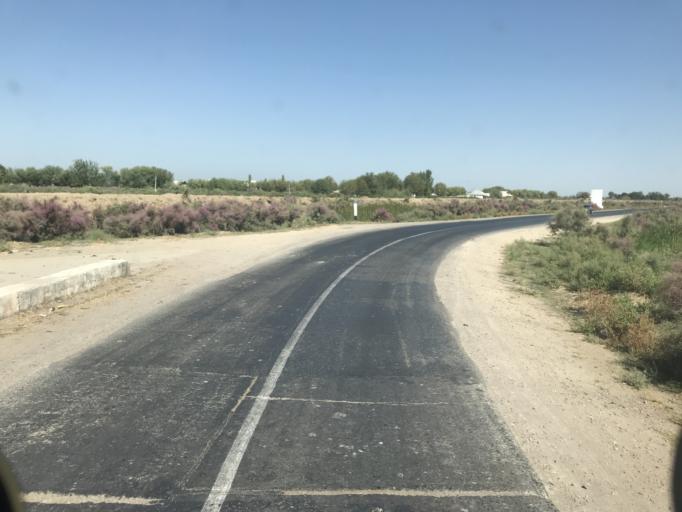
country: KZ
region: Ongtustik Qazaqstan
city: Myrzakent
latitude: 40.7498
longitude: 68.5371
